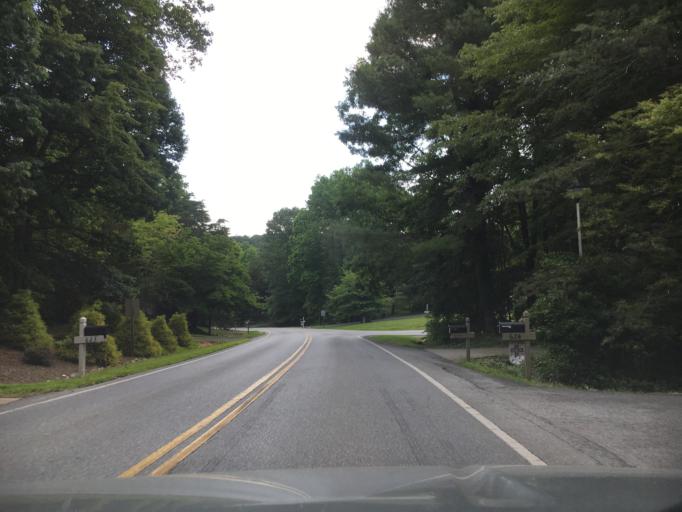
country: US
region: Virginia
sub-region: Bedford County
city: Forest
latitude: 37.3851
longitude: -79.2595
